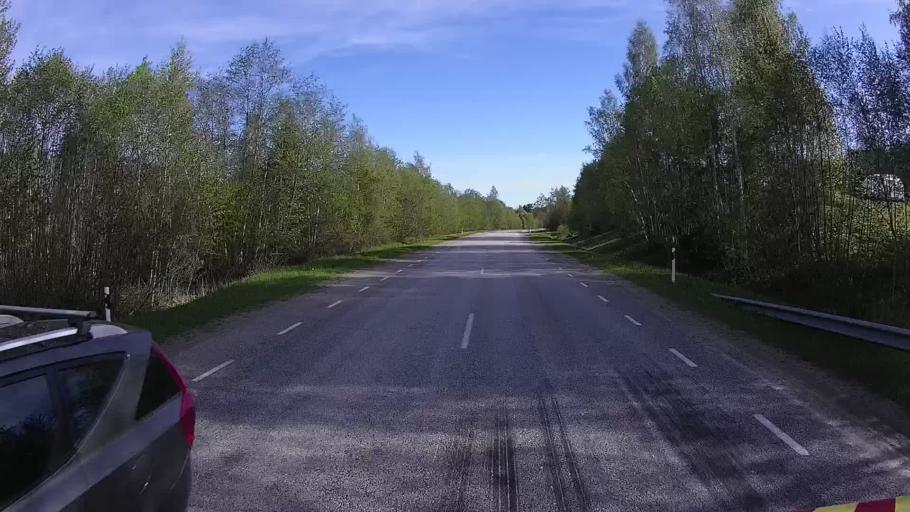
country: EE
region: Tartu
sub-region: Noo vald
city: Noo
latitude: 58.1493
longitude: 26.5257
